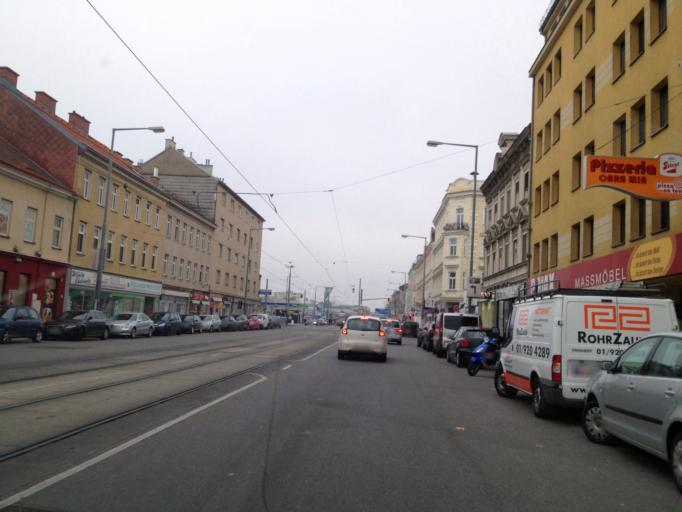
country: AT
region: Lower Austria
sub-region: Politischer Bezirk Korneuburg
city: Langenzersdorf
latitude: 48.2671
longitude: 16.3927
